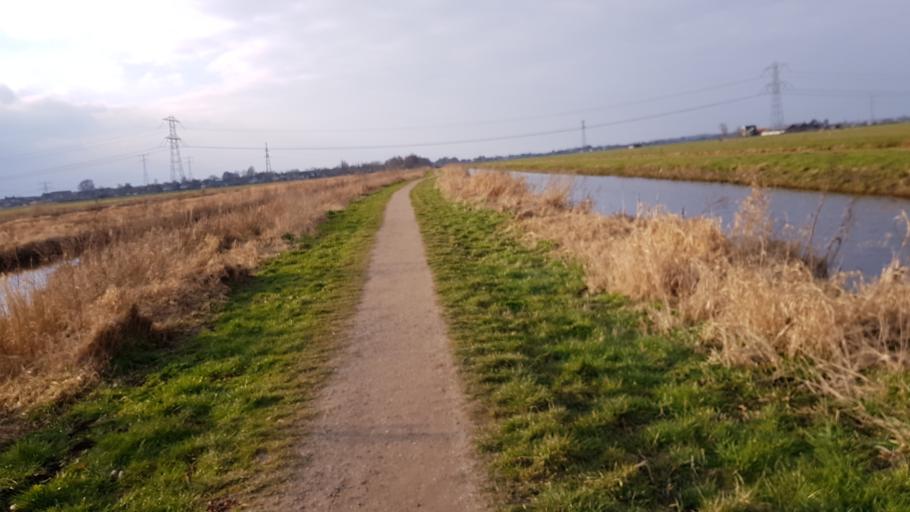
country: NL
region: South Holland
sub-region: Molenwaard
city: Nieuw-Lekkerland
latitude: 51.9251
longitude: 4.6563
